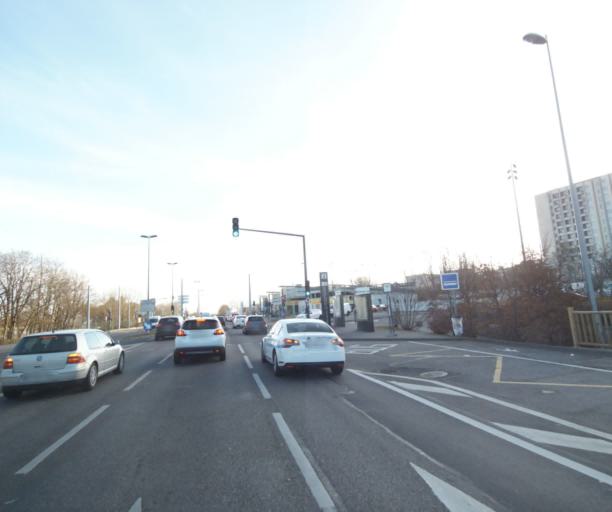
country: FR
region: Lorraine
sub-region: Departement de Meurthe-et-Moselle
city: Villers-les-Nancy
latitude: 48.6485
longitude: 6.1444
